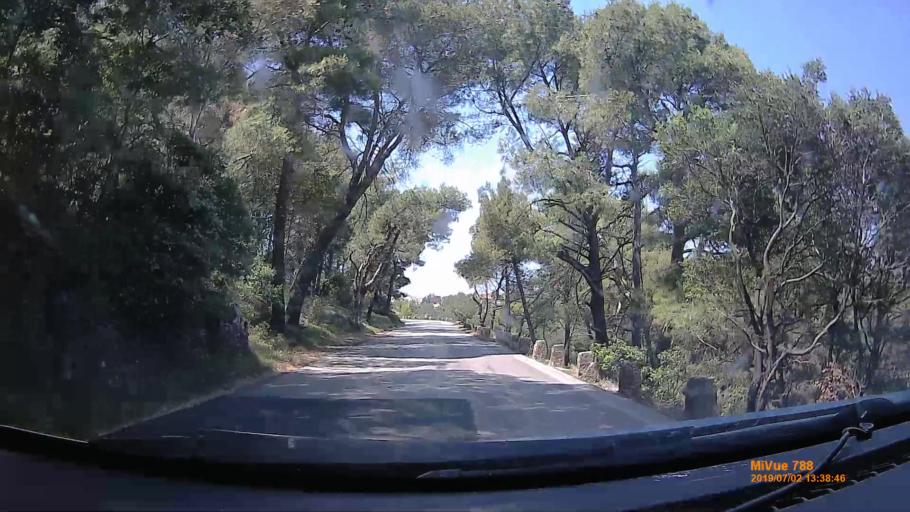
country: HR
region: Primorsko-Goranska
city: Mali Losinj
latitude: 44.5258
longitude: 14.4816
